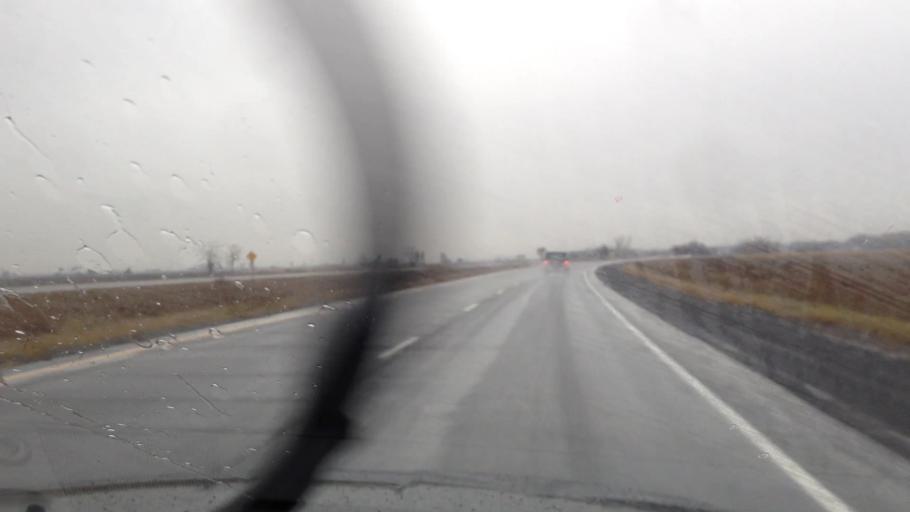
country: CA
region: Ontario
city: Casselman
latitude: 45.3584
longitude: -74.8833
